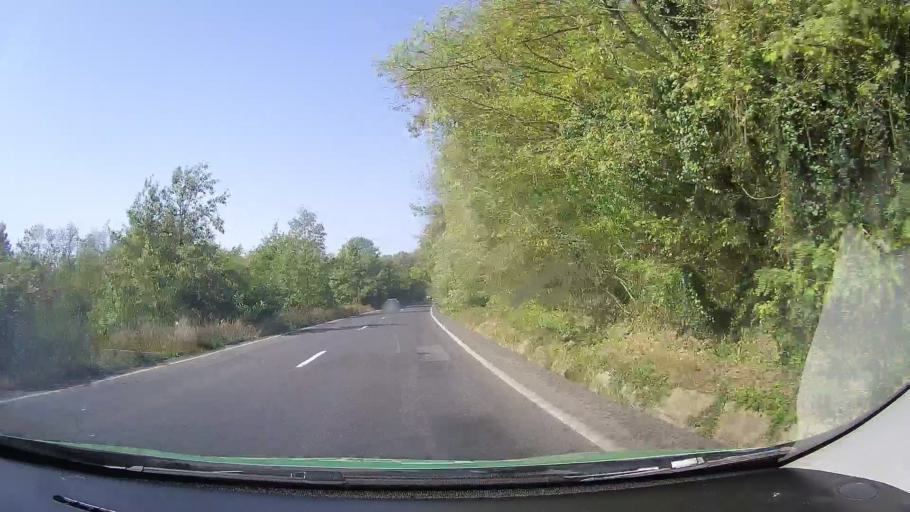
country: RO
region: Arad
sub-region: Comuna Savarsin
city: Savarsin
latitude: 46.0144
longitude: 22.2594
